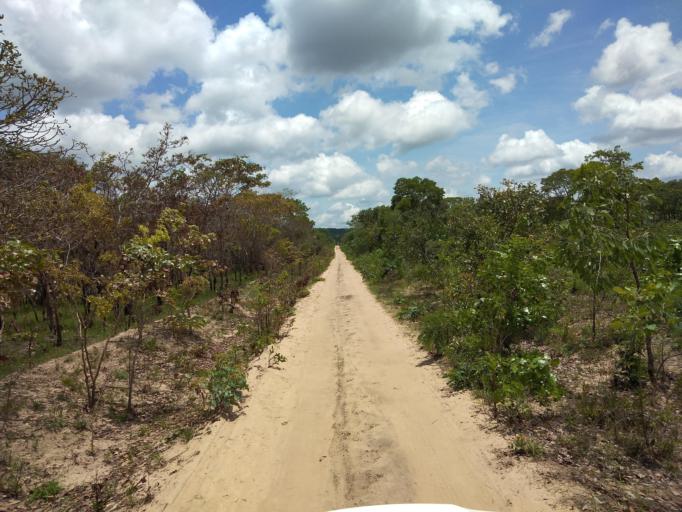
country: ZM
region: Central
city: Mkushi
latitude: -13.8940
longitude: 29.8503
